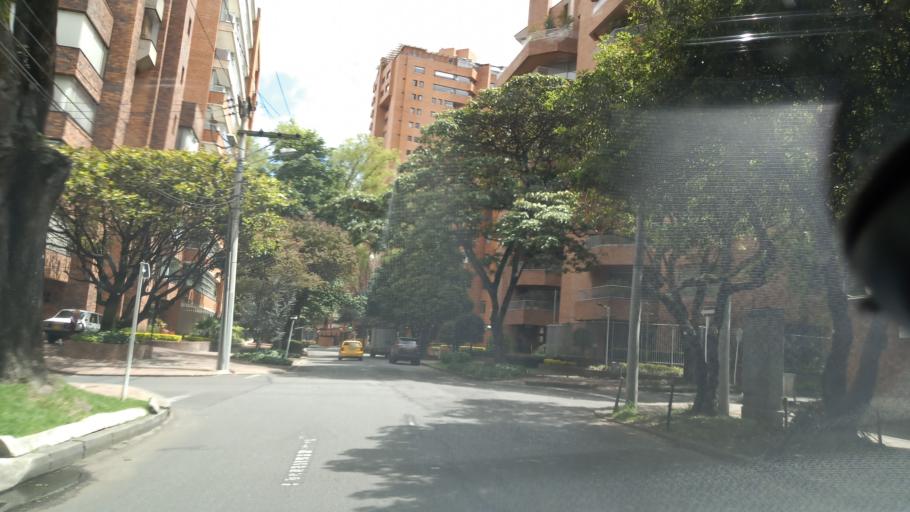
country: CO
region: Bogota D.C.
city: Barrio San Luis
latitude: 4.6655
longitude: -74.0499
